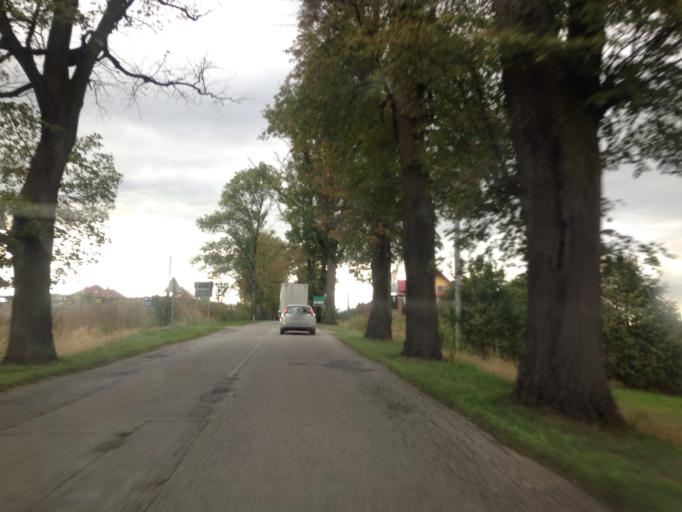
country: PL
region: Pomeranian Voivodeship
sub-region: Powiat kwidzynski
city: Kwidzyn
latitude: 53.7300
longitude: 19.0400
